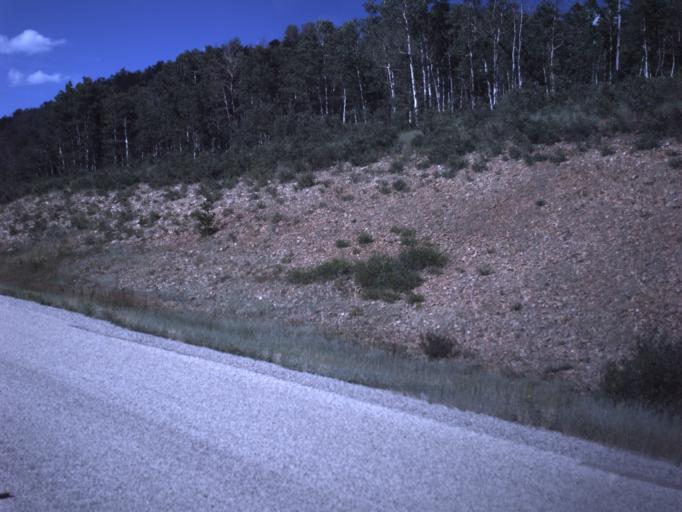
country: US
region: Utah
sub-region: Wasatch County
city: Heber
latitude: 40.2974
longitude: -111.2520
